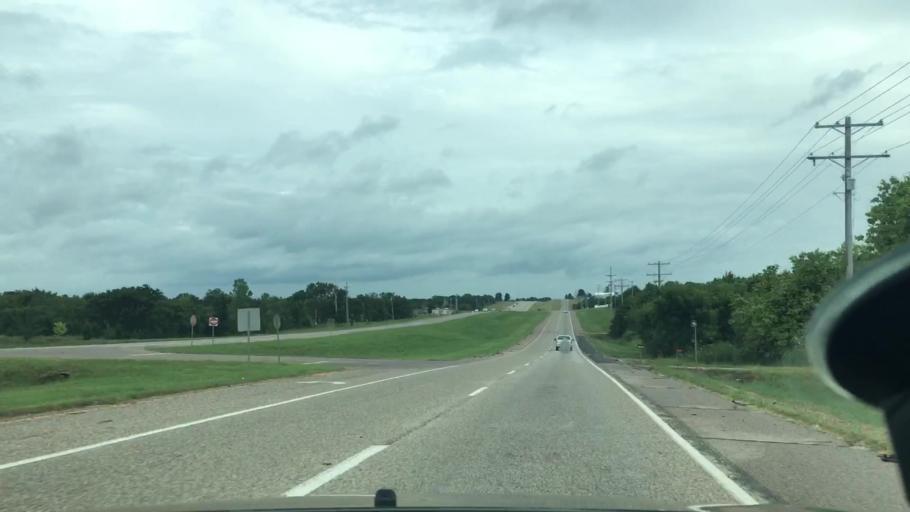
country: US
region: Oklahoma
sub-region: Seminole County
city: Seminole
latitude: 35.2842
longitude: -96.6712
